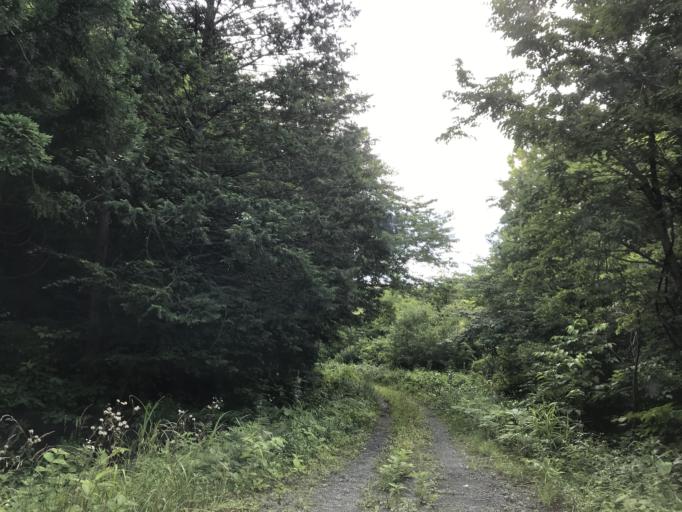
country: JP
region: Iwate
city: Ichinoseki
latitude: 38.9059
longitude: 140.9511
